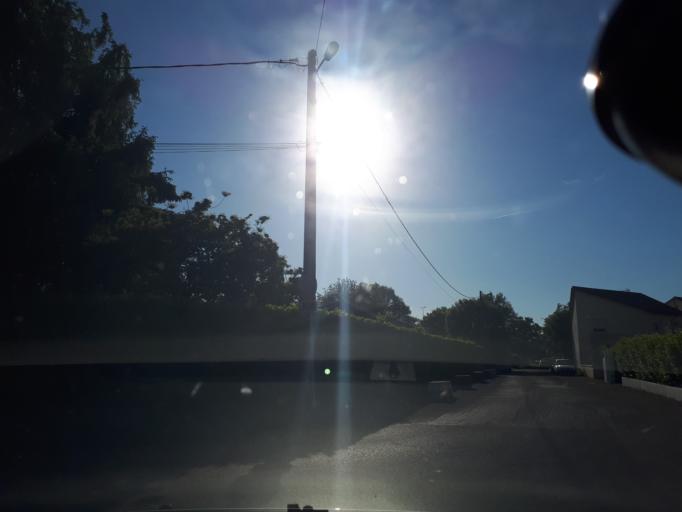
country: FR
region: Rhone-Alpes
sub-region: Departement de l'Isere
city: Bourgoin-Jallieu
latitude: 45.5980
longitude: 5.2690
